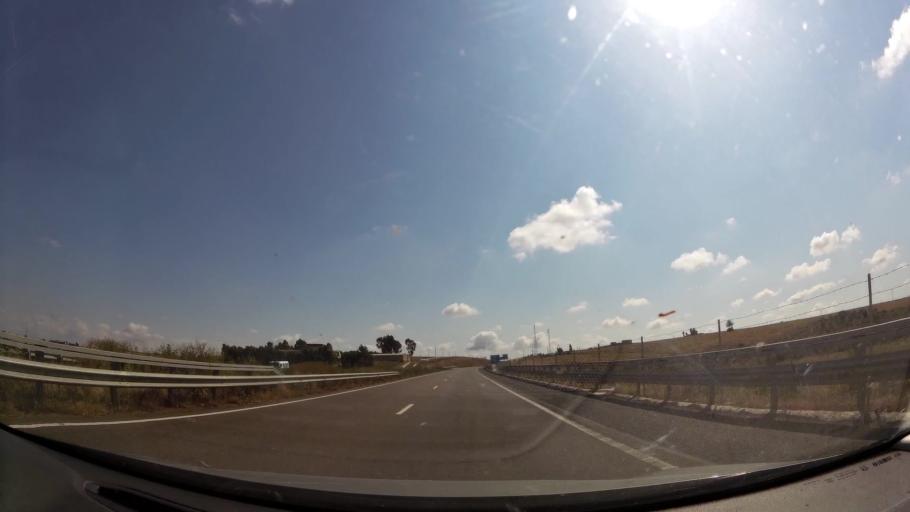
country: MA
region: Rabat-Sale-Zemmour-Zaer
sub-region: Skhirate-Temara
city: Temara
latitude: 33.8532
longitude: -6.8261
